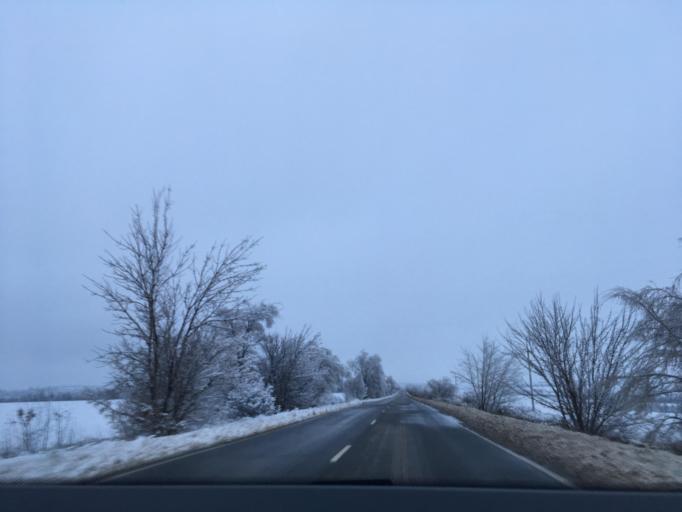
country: RU
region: Voronezj
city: Verkhniy Mamon
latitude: 50.0201
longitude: 40.1112
